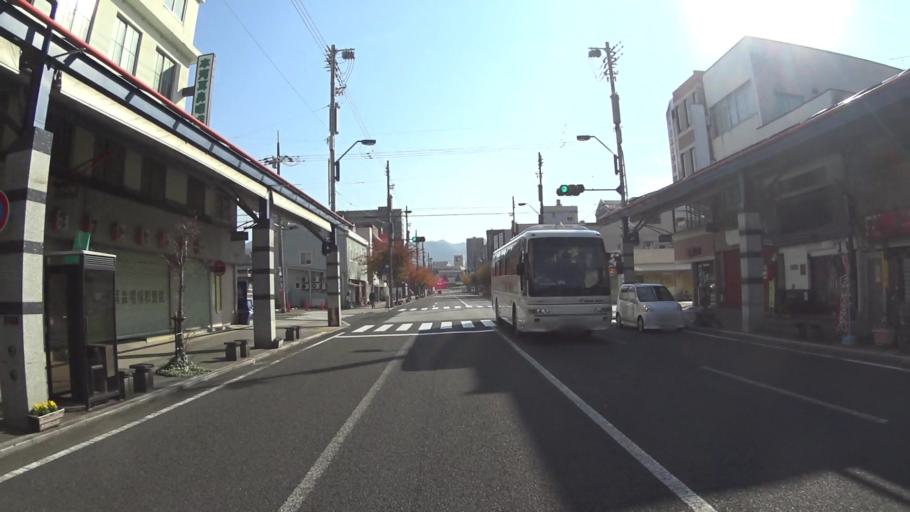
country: JP
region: Kyoto
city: Maizuru
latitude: 35.4720
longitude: 135.3936
